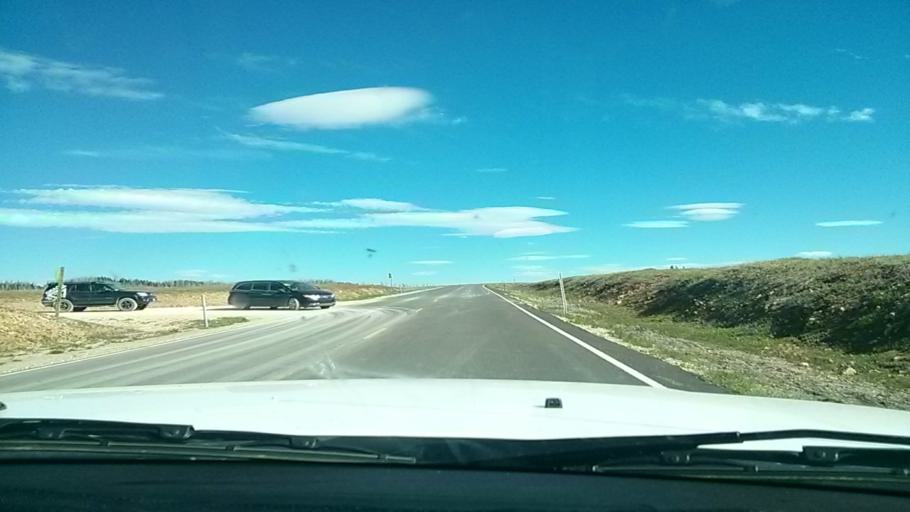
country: US
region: Utah
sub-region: Iron County
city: Parowan
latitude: 37.6702
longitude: -112.8401
